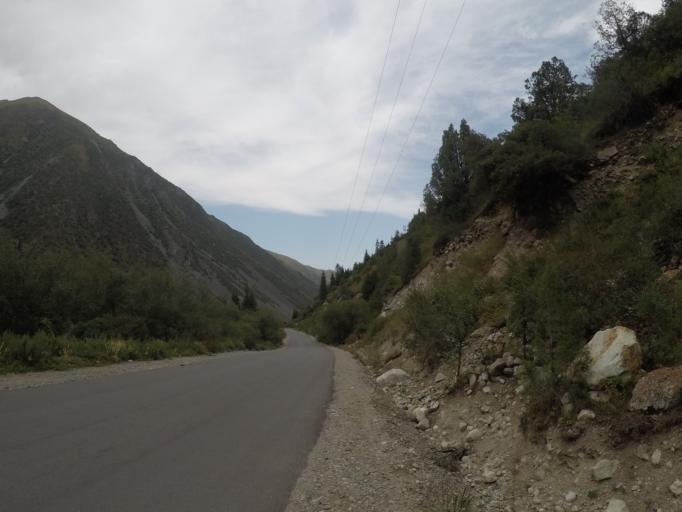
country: KG
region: Chuy
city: Bishkek
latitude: 42.5736
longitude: 74.4830
